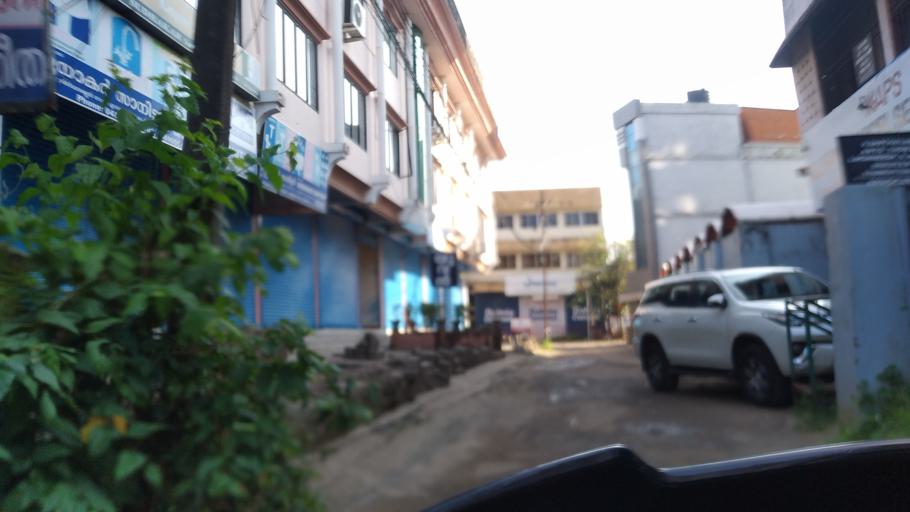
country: IN
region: Kerala
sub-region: Ernakulam
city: Cochin
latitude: 9.9795
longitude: 76.2824
